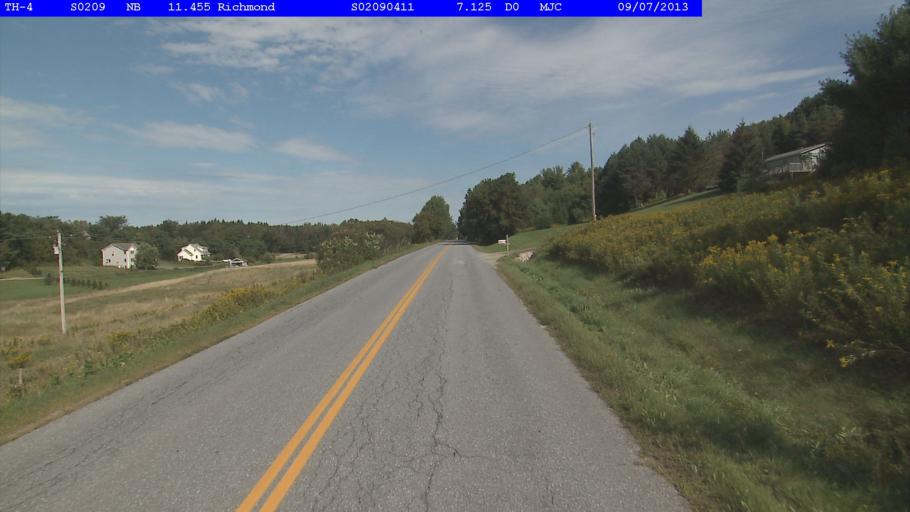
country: US
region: Vermont
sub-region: Chittenden County
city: Jericho
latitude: 44.4265
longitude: -72.9814
